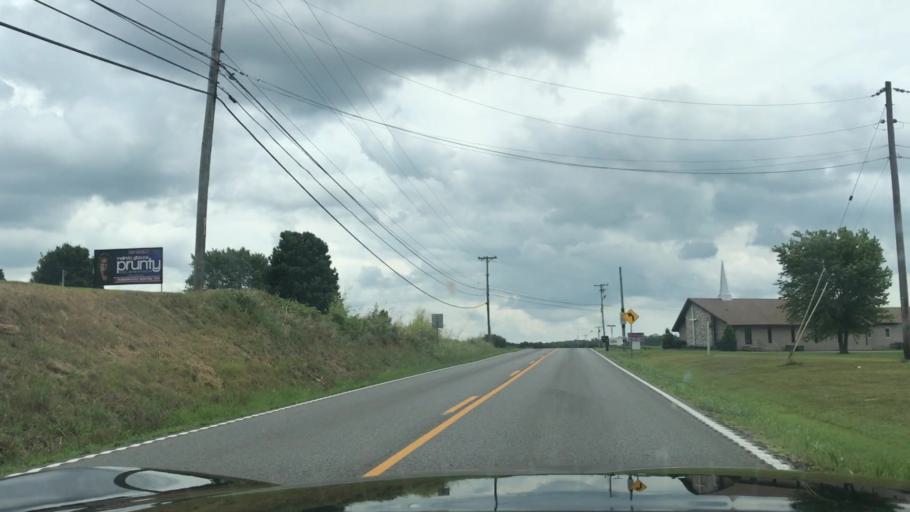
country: US
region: Kentucky
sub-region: Muhlenberg County
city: Greenville
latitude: 37.1993
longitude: -87.1331
